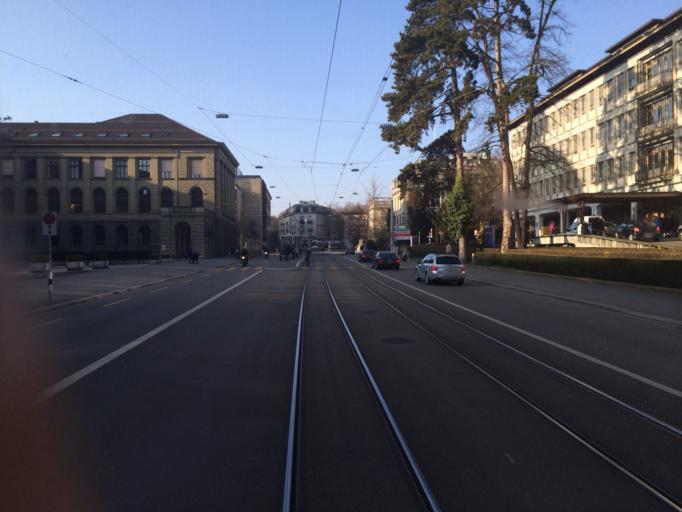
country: CH
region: Zurich
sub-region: Bezirk Zuerich
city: Zuerich (Kreis 1) / Rathaus
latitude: 47.3763
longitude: 8.5488
